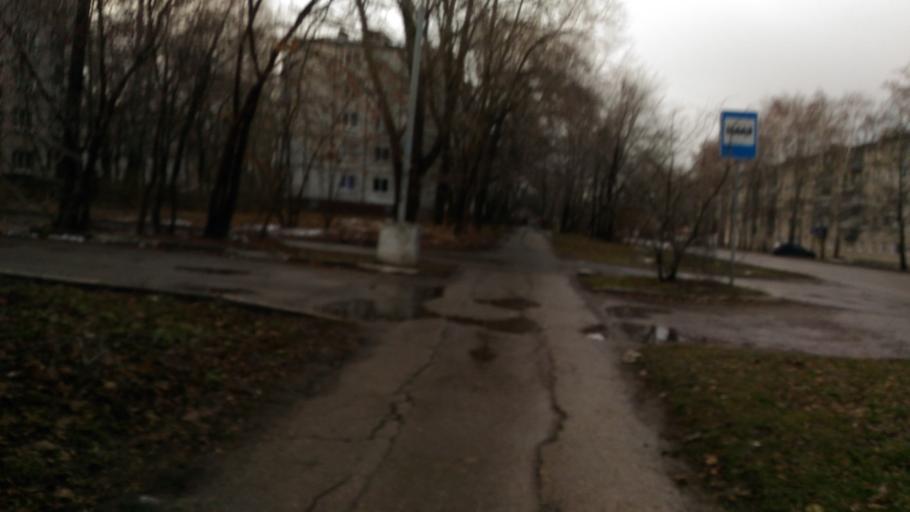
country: RU
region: Ulyanovsk
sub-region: Ulyanovskiy Rayon
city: Ulyanovsk
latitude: 54.3479
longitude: 48.3895
